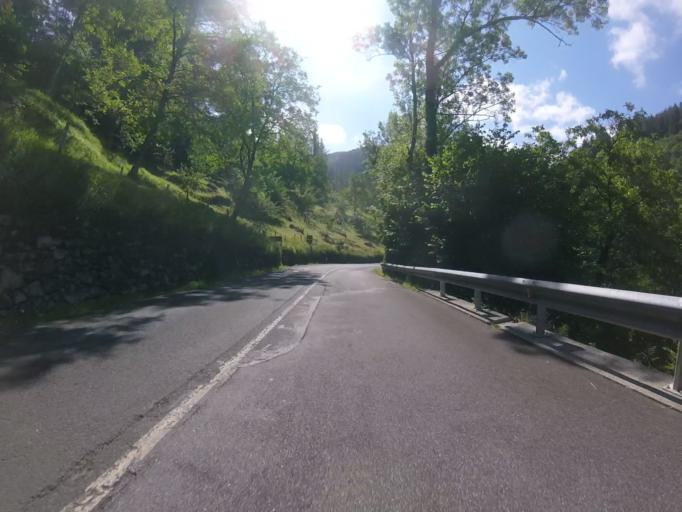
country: ES
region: Basque Country
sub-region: Provincia de Guipuzcoa
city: Beizama
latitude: 43.0982
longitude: -2.2394
